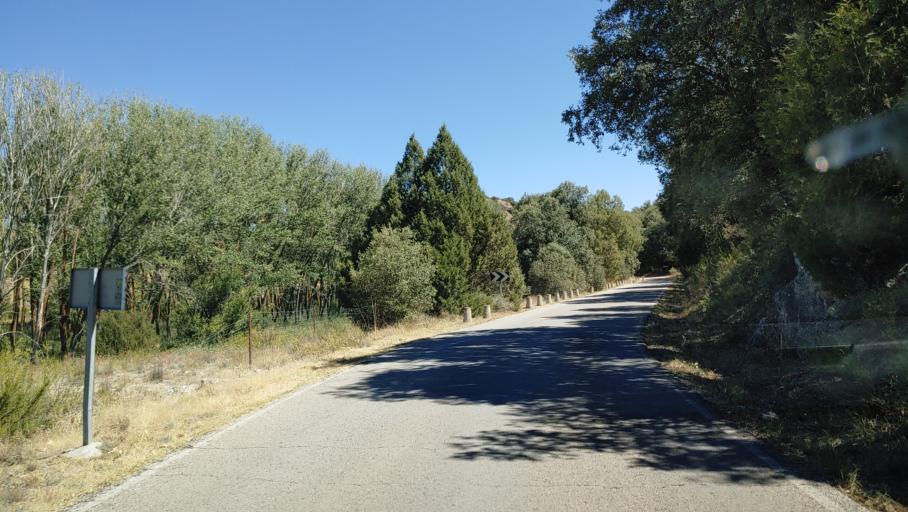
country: ES
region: Castille-La Mancha
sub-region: Provincia de Ciudad Real
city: Ruidera
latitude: 38.9255
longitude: -2.8363
